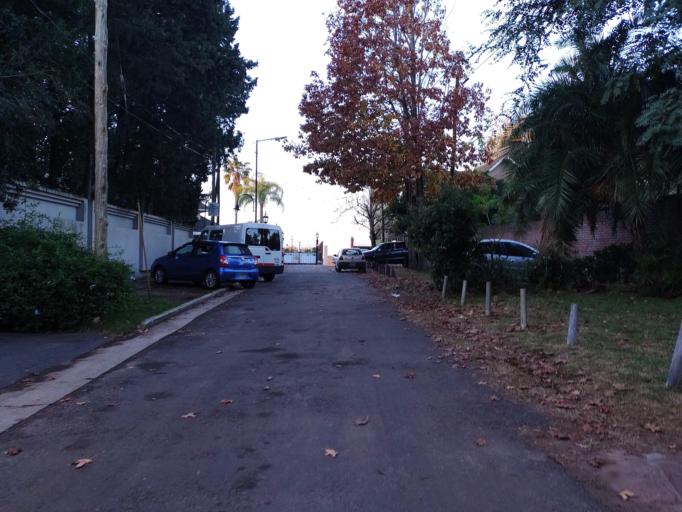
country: AR
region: Buenos Aires
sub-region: Partido de San Isidro
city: San Isidro
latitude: -34.4464
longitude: -58.5391
